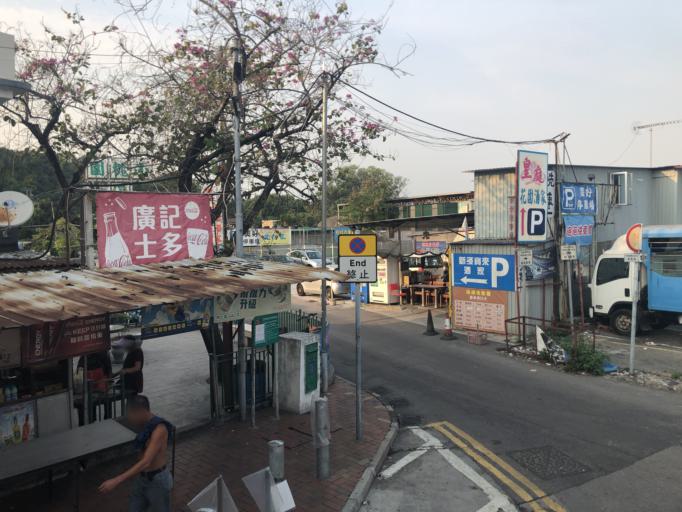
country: HK
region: Yuen Long
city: Yuen Long Kau Hui
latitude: 22.4676
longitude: 113.9840
